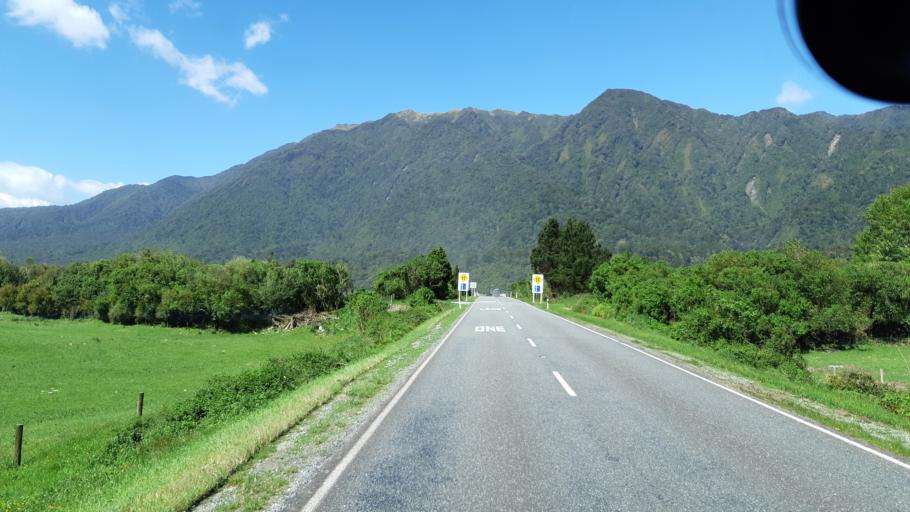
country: NZ
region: West Coast
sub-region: Westland District
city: Hokitika
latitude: -43.1556
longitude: 170.6180
